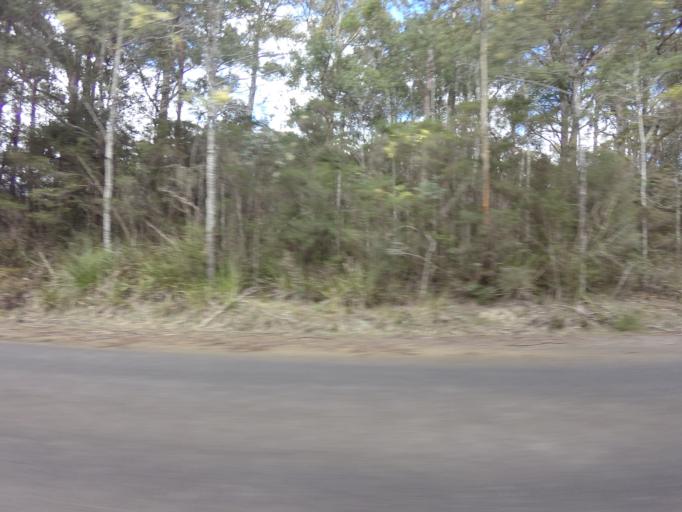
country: AU
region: Tasmania
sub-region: Huon Valley
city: Geeveston
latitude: -43.4133
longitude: 146.9175
